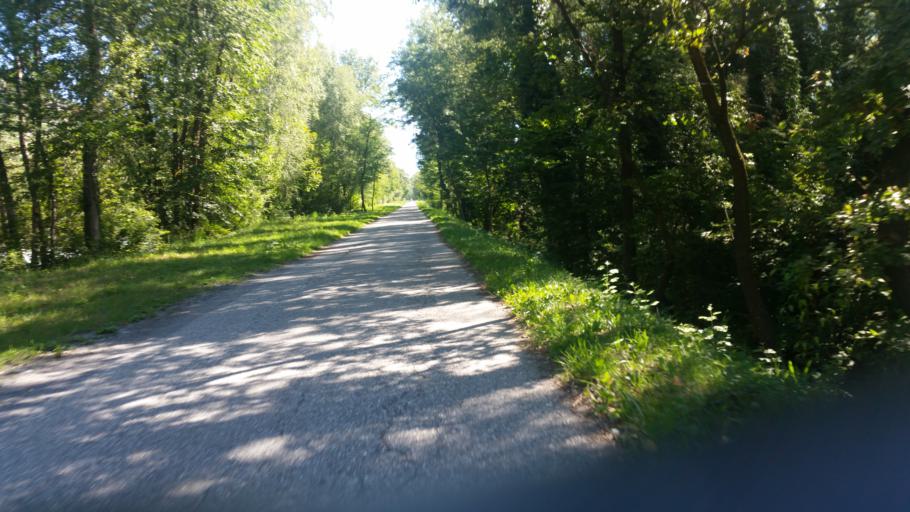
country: CH
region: Valais
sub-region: Sierre District
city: Chermignon-d'en Haut
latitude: 46.2686
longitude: 7.4749
